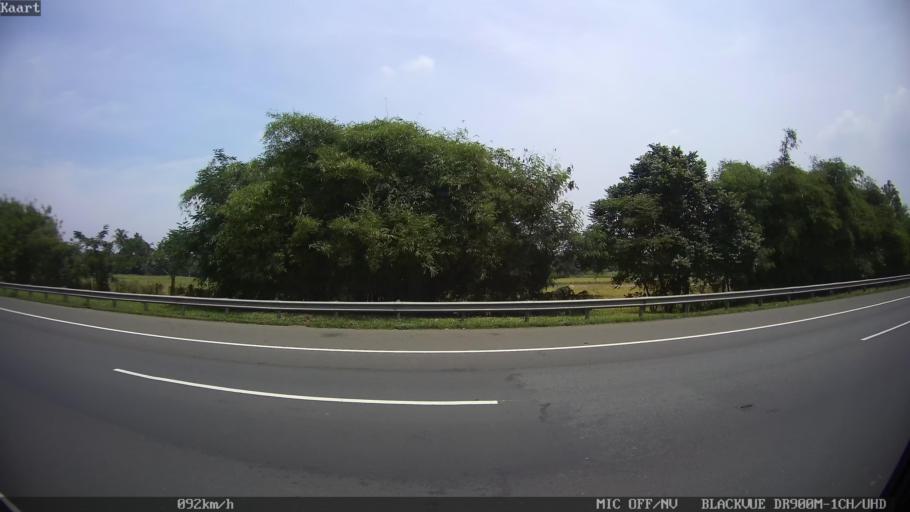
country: ID
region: West Java
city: Kresek
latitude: -6.1772
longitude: 106.3831
